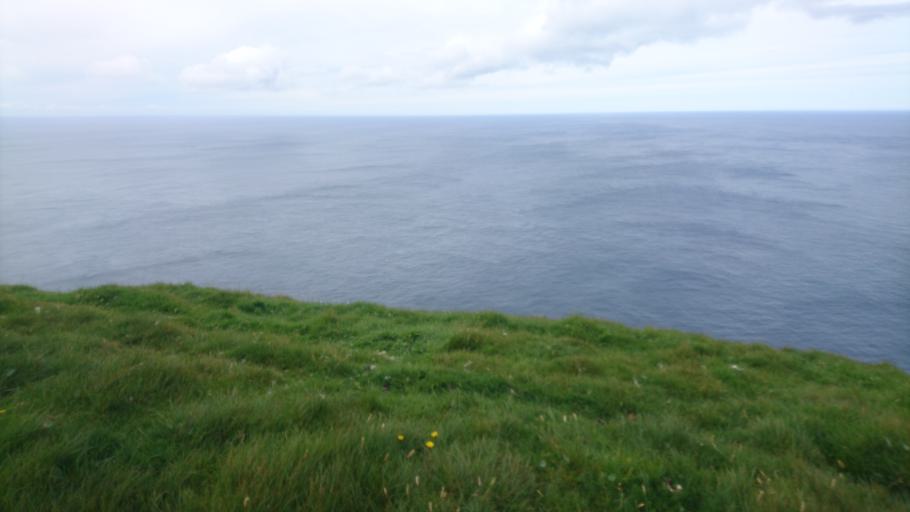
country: FO
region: Vagar
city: Sorvagur
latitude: 62.1133
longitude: -7.6234
